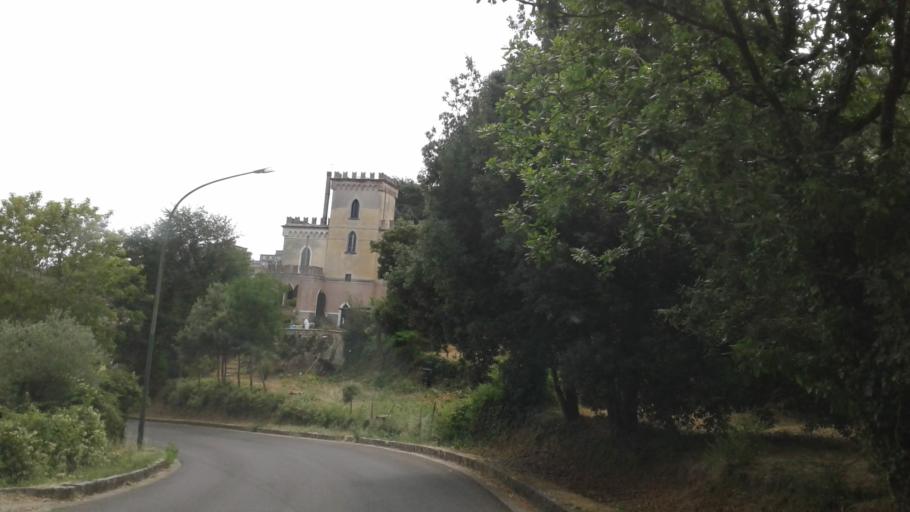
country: IT
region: Sardinia
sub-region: Provincia di Olbia-Tempio
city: Tempio Pausania
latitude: 40.9000
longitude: 9.0955
